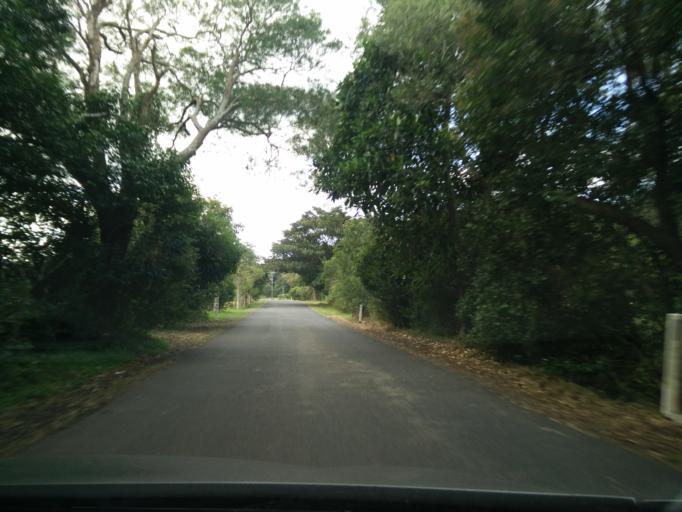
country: AU
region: New South Wales
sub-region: Kiama
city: Jamberoo
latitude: -34.6657
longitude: 150.7912
